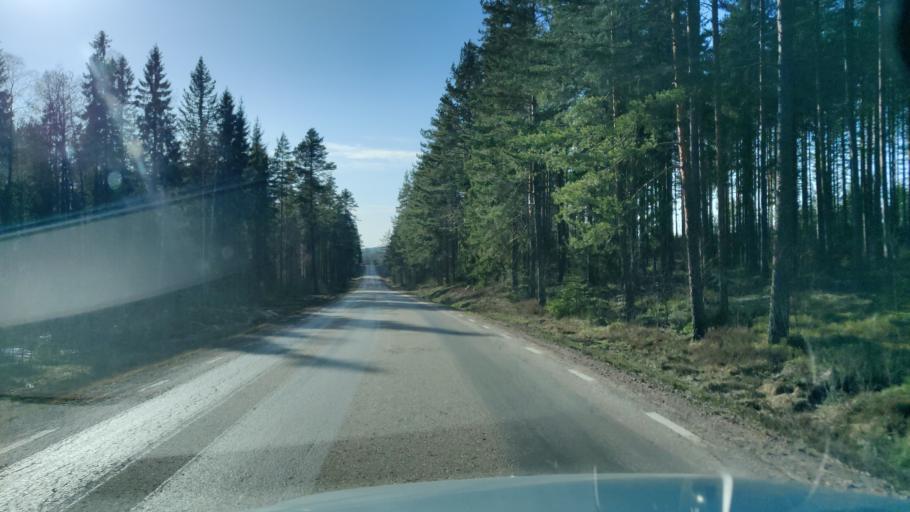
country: SE
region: Vaermland
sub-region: Sunne Kommun
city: Sunne
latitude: 59.9926
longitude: 13.3042
